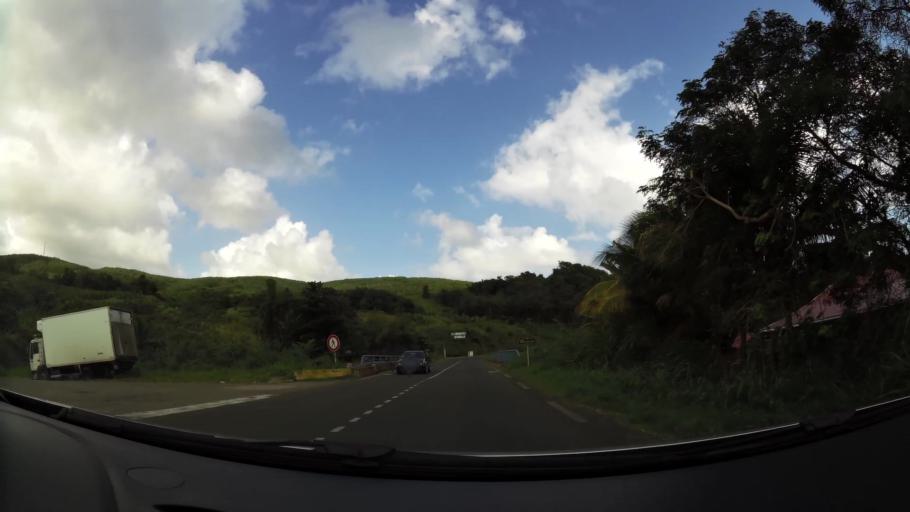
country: MQ
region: Martinique
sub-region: Martinique
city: Le Lorrain
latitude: 14.8264
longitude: -61.0422
